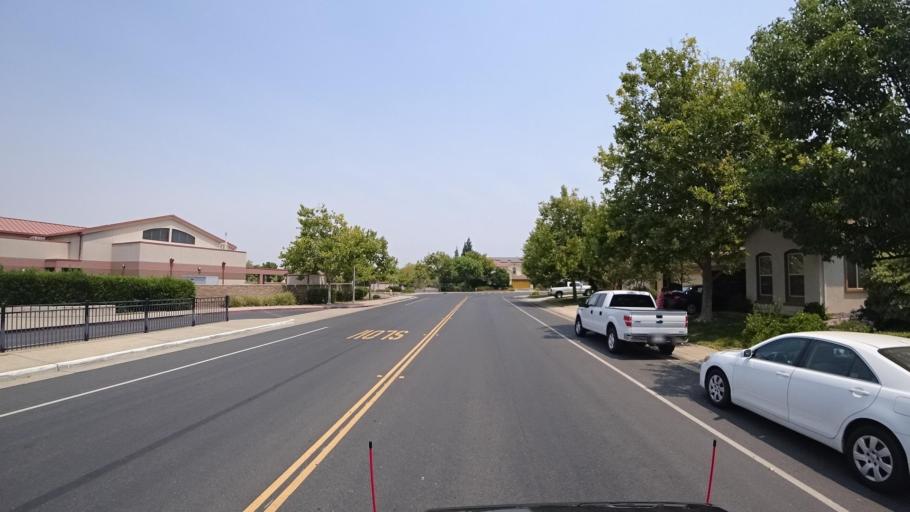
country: US
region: California
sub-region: Placer County
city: Rocklin
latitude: 38.7982
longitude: -121.2794
